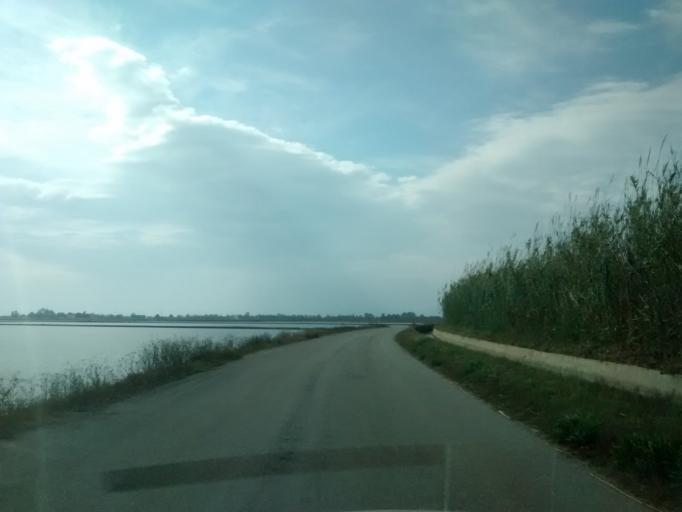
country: ES
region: Catalonia
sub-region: Provincia de Tarragona
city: Deltebre
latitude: 40.6990
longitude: 0.8281
